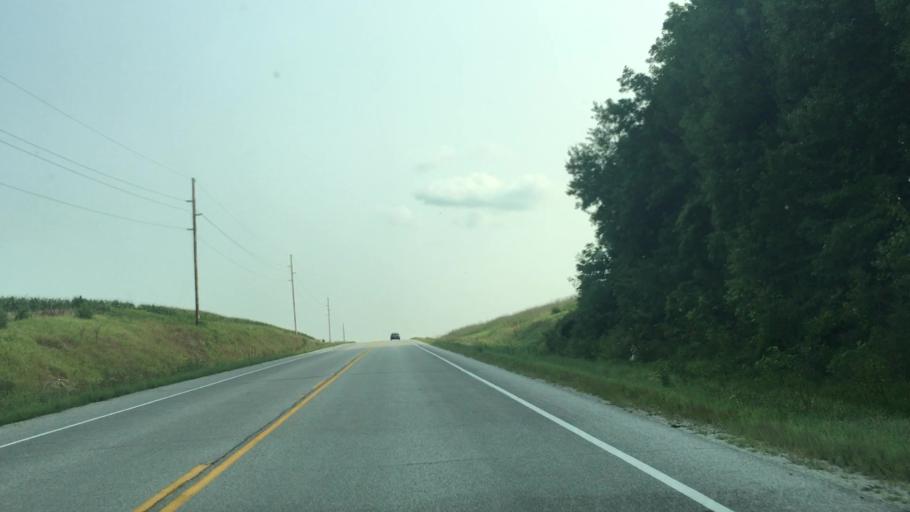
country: US
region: Minnesota
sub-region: Fillmore County
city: Harmony
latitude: 43.5736
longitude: -91.9299
